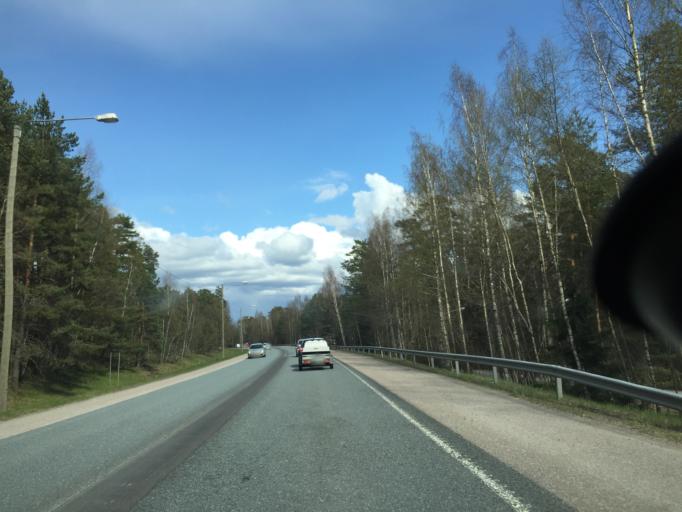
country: FI
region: Uusimaa
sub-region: Raaseporin
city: Ekenaes
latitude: 59.9894
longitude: 23.4916
